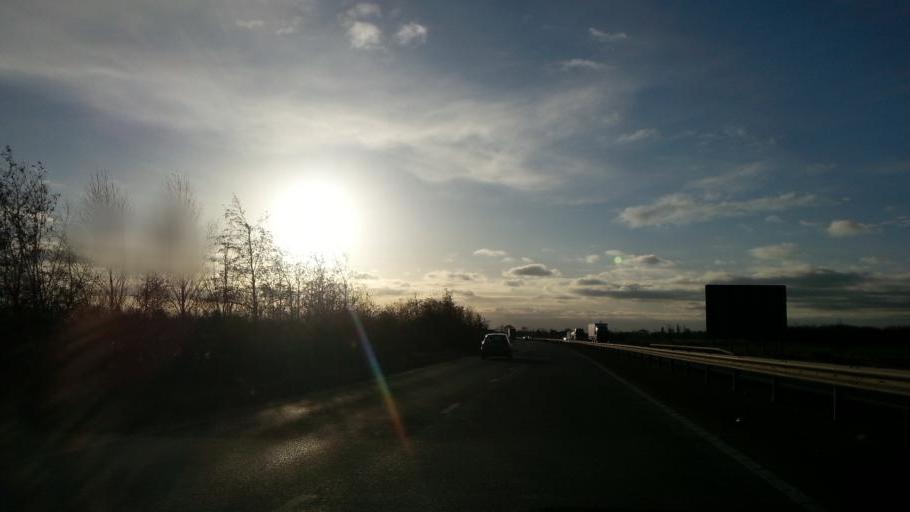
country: GB
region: England
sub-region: Peterborough
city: Thorney
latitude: 52.6257
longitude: -0.1123
